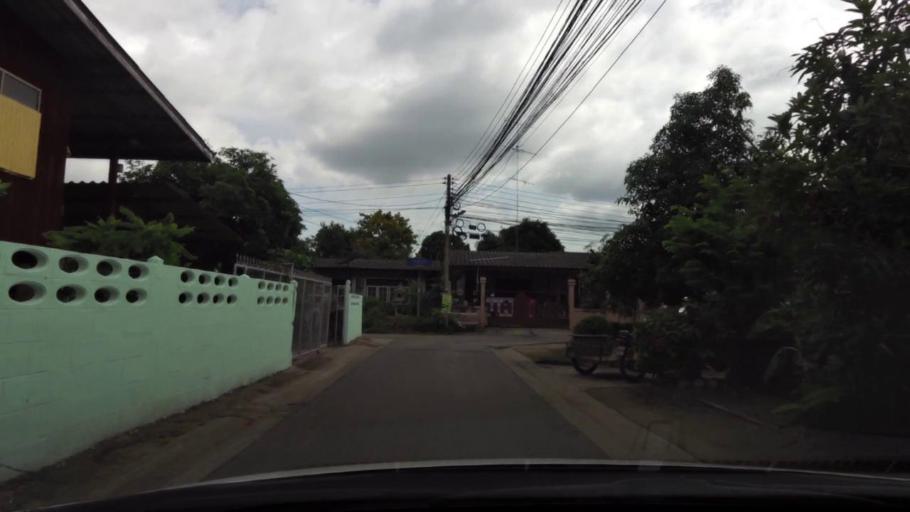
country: TH
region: Ratchaburi
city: Ratchaburi
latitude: 13.5325
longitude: 99.8313
